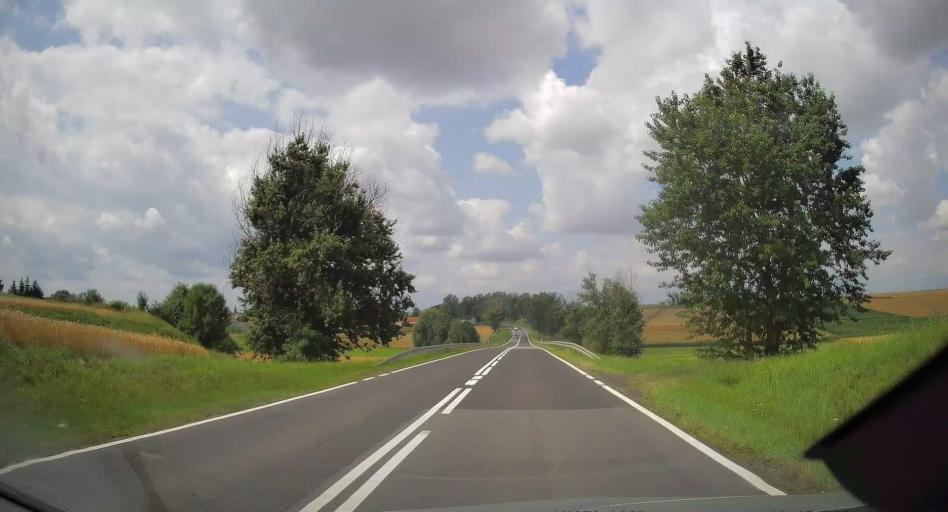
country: PL
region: Opole Voivodeship
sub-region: Powiat prudnicki
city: Raclawice Slaskie
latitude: 50.3458
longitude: 17.7496
